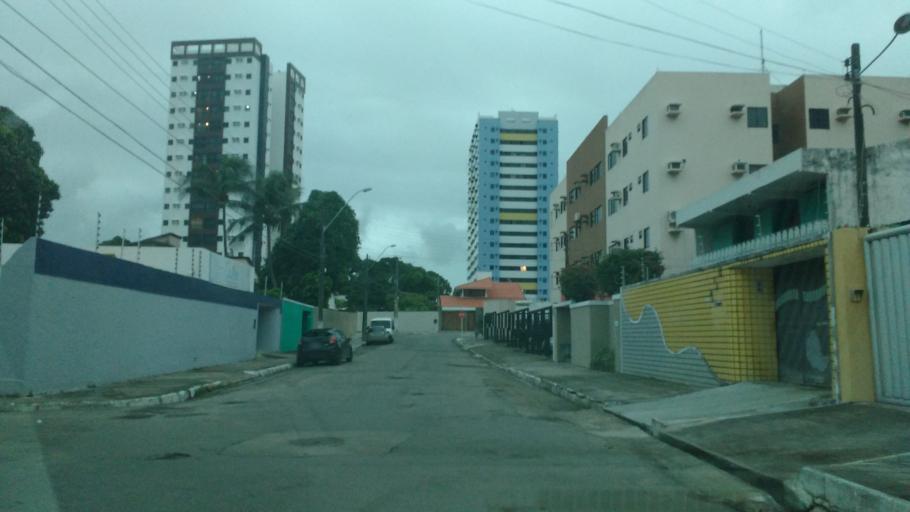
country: BR
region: Alagoas
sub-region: Maceio
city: Maceio
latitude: -9.6359
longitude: -35.7396
